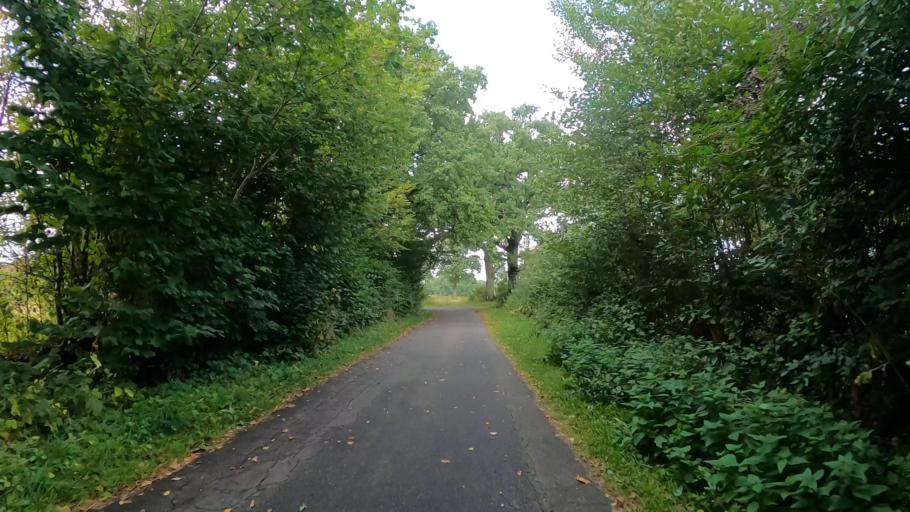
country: DE
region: Schleswig-Holstein
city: Kolln-Reisiek
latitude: 53.7313
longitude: 9.6830
